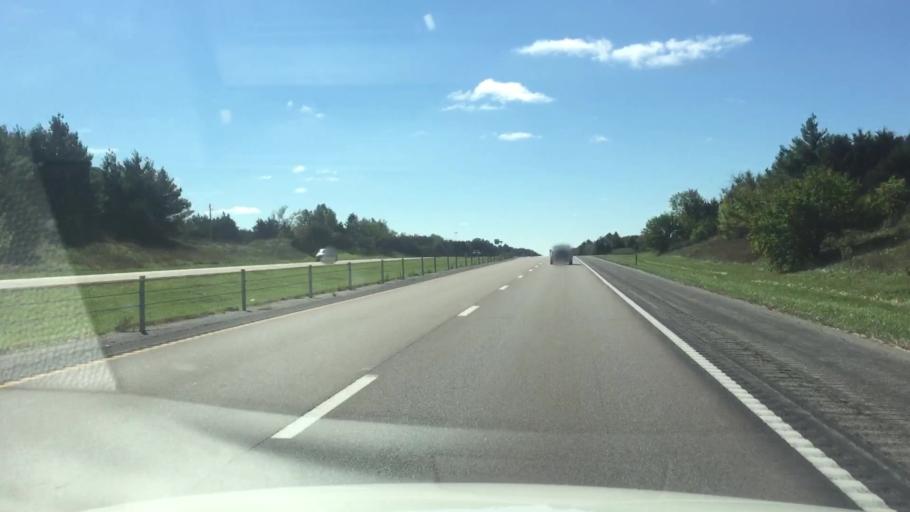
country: US
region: Missouri
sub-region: Boone County
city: Ashland
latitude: 38.7434
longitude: -92.2537
